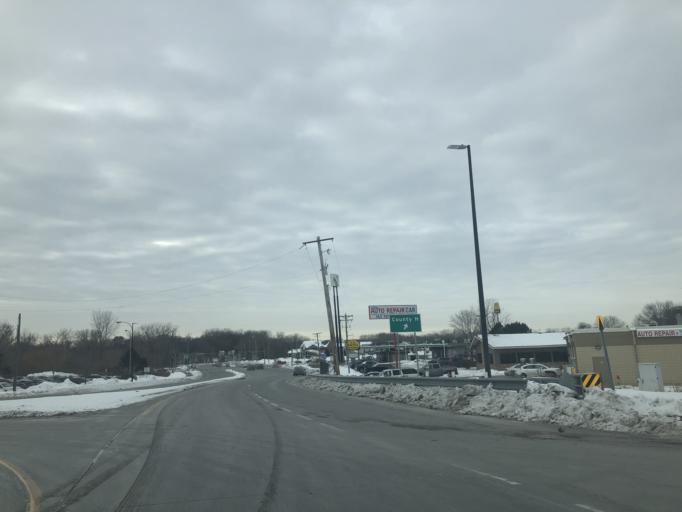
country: US
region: Minnesota
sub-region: Ramsey County
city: Mounds View
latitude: 45.0959
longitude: -93.1902
